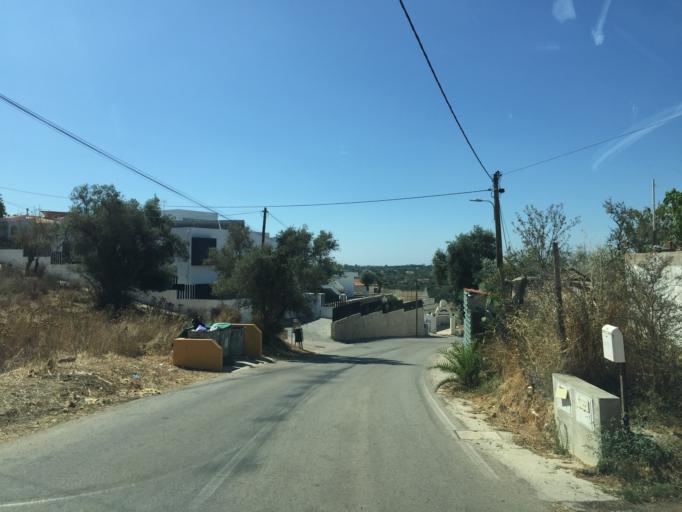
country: PT
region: Faro
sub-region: Loule
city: Vilamoura
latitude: 37.1167
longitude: -8.0987
